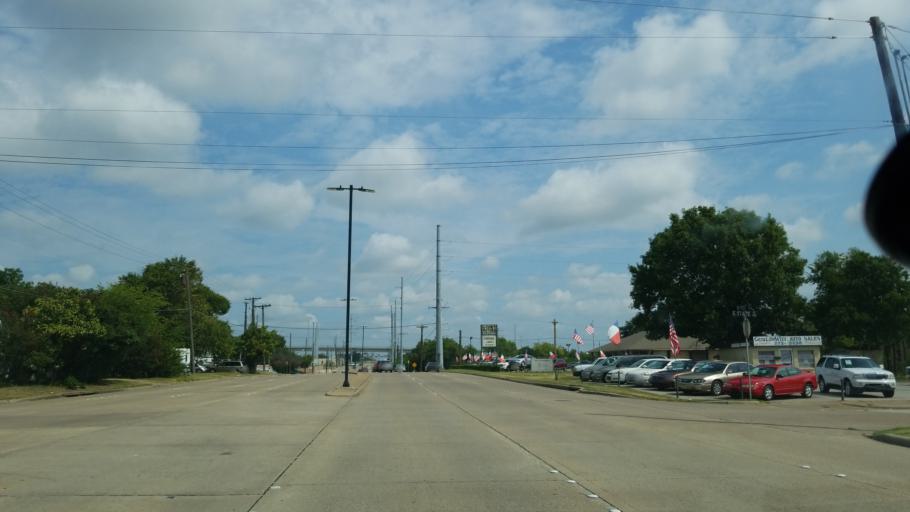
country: US
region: Texas
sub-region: Dallas County
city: Garland
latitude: 32.9132
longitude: -96.6307
